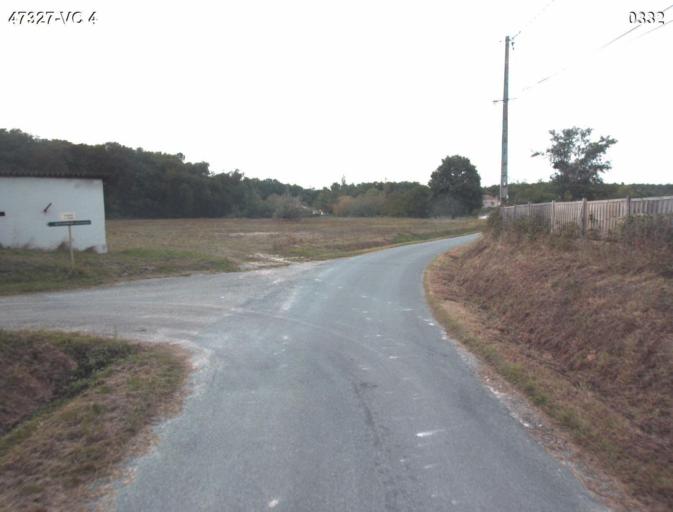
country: FR
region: Aquitaine
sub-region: Departement du Lot-et-Garonne
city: Barbaste
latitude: 44.2121
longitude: 0.2566
